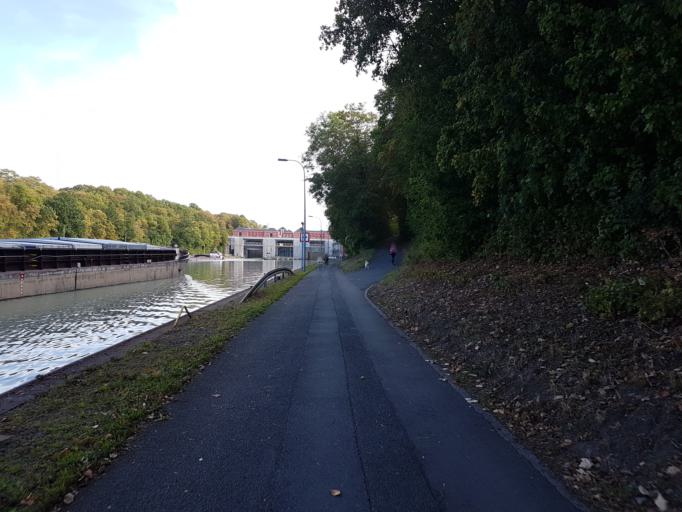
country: DE
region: Lower Saxony
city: Laatzen
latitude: 52.3641
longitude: 9.8605
